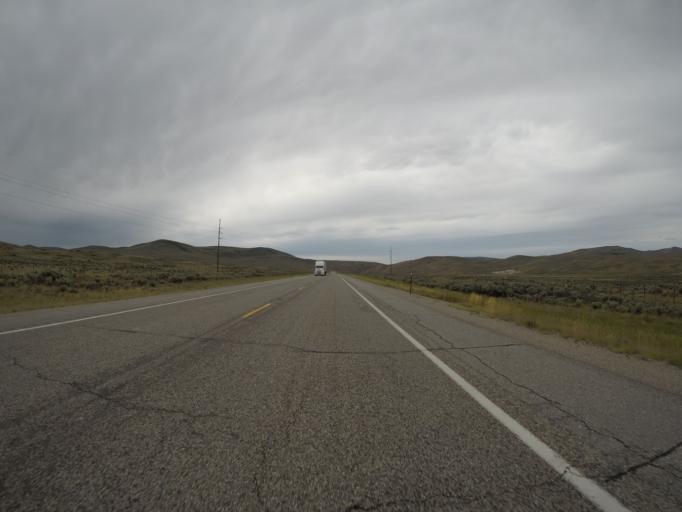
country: US
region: Wyoming
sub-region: Lincoln County
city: Kemmerer
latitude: 41.8170
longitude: -110.7785
